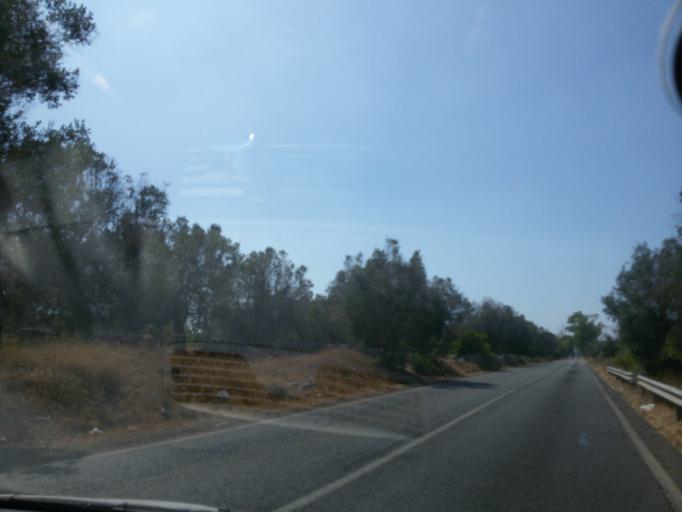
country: IT
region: Apulia
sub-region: Provincia di Lecce
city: Porto Cesareo
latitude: 40.2377
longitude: 17.9524
